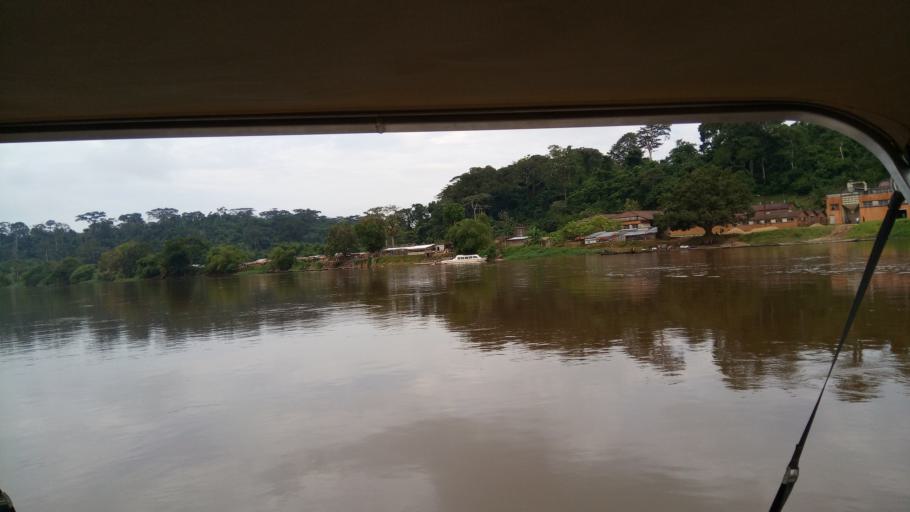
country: CD
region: Eastern Province
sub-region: Sous-Region de la Tshopo
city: Yangambi
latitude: 0.7551
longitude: 24.4852
